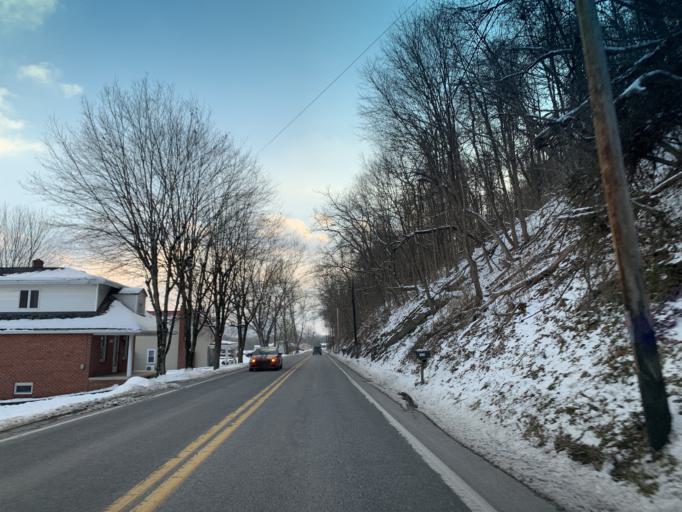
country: US
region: Maryland
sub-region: Allegany County
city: Cumberland
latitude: 39.7497
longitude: -78.7524
